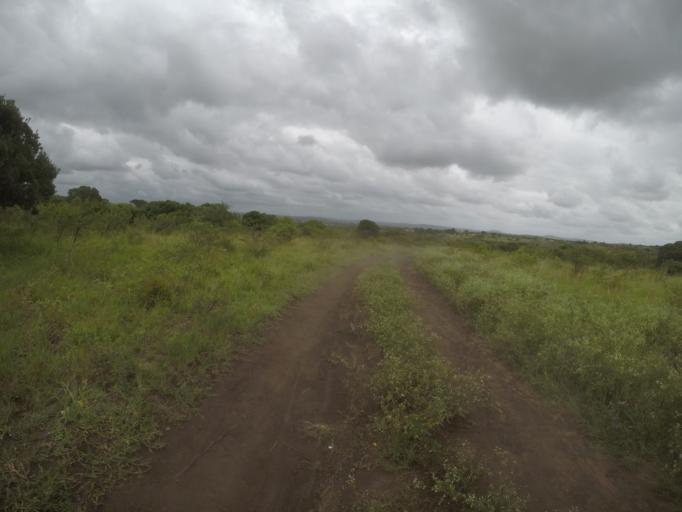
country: ZA
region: KwaZulu-Natal
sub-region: uThungulu District Municipality
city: Empangeni
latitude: -28.5590
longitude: 31.8834
